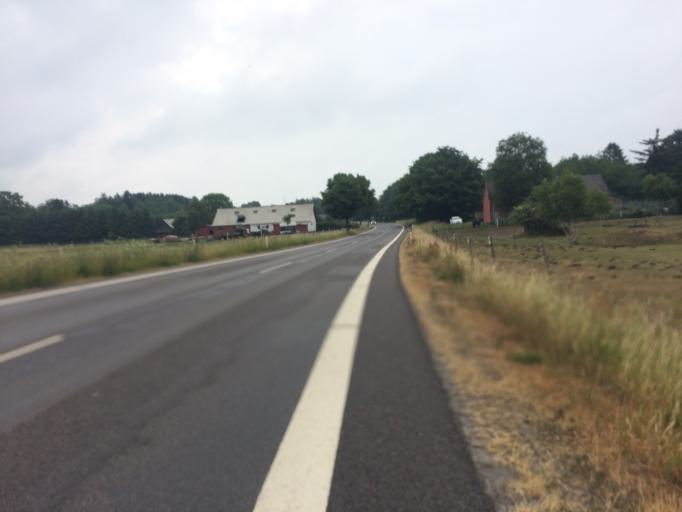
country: DK
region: Capital Region
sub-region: Bornholm Kommune
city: Akirkeby
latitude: 55.1486
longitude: 14.8816
